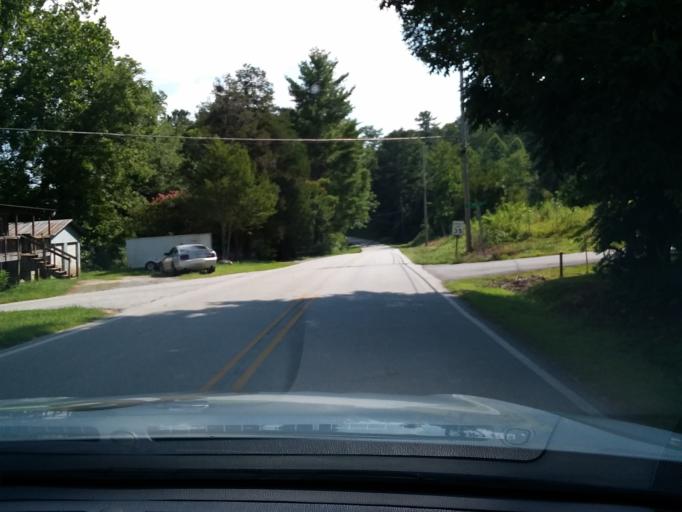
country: US
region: Georgia
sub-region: Rabun County
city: Clayton
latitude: 34.8460
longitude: -83.4341
